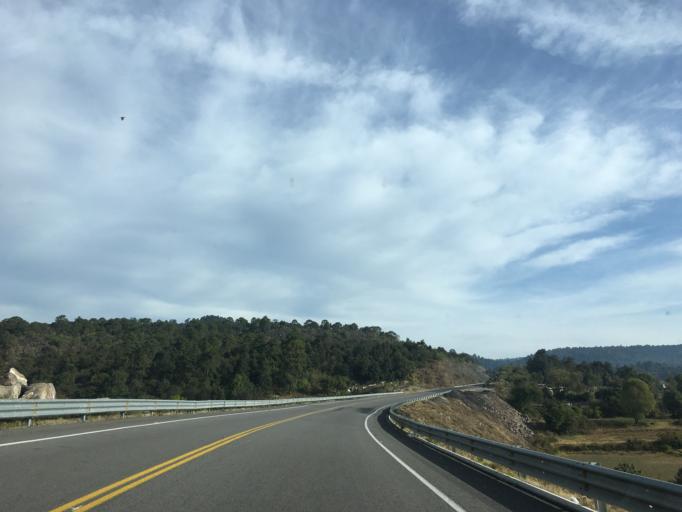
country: MX
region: Mexico
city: San Bartolo
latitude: 19.2545
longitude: -100.0678
